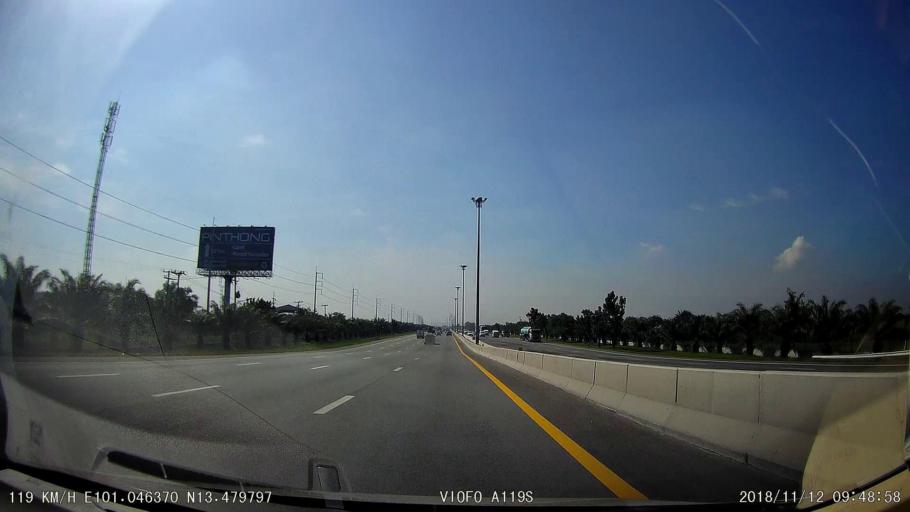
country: TH
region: Chon Buri
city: Phan Thong
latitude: 13.4776
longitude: 101.0463
